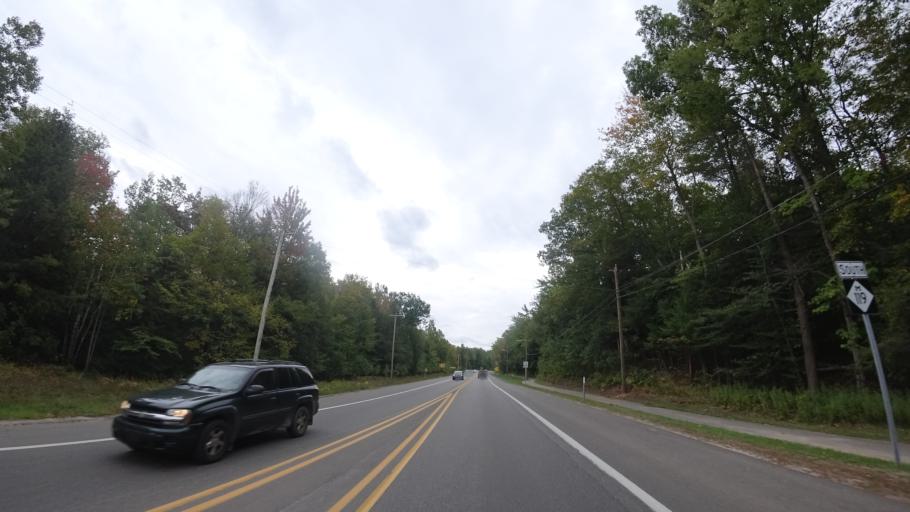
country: US
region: Michigan
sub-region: Emmet County
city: Petoskey
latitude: 45.4130
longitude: -84.9042
